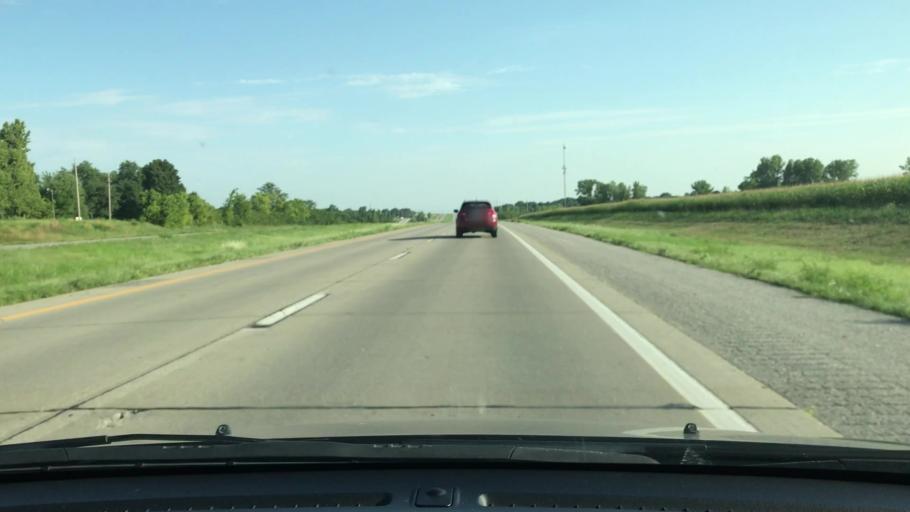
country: US
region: Missouri
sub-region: Jackson County
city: Lees Summit
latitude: 38.8755
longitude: -94.3747
